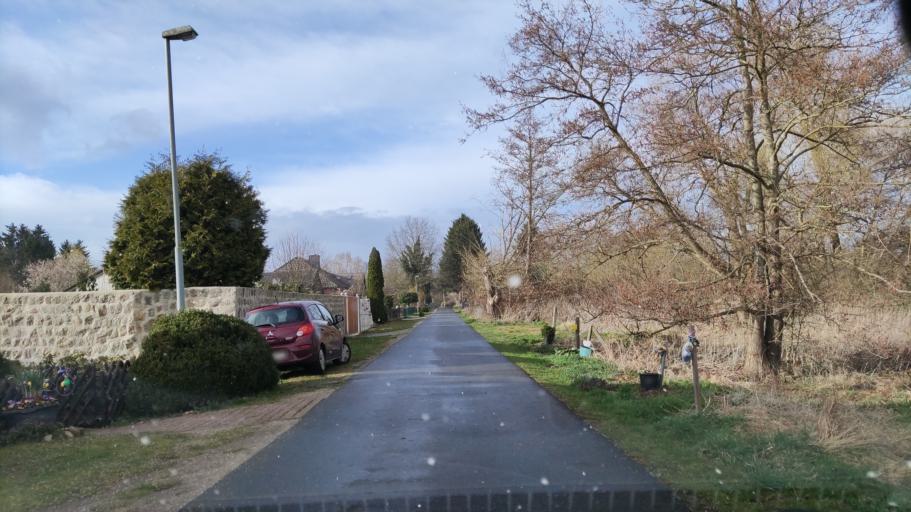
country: DE
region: Lower Saxony
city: Dahlenburg
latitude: 53.1841
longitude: 10.7373
